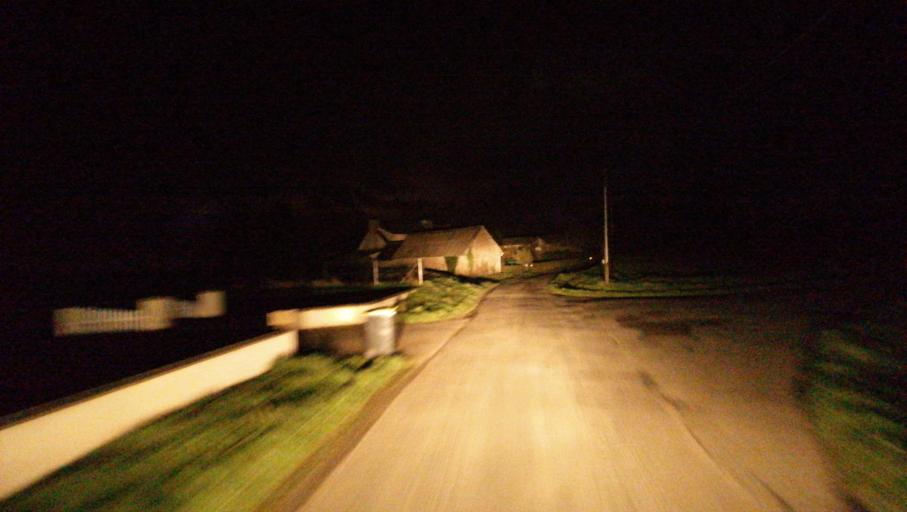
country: FR
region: Brittany
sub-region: Departement des Cotes-d'Armor
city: Saint-Agathon
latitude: 48.5804
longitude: -3.0828
